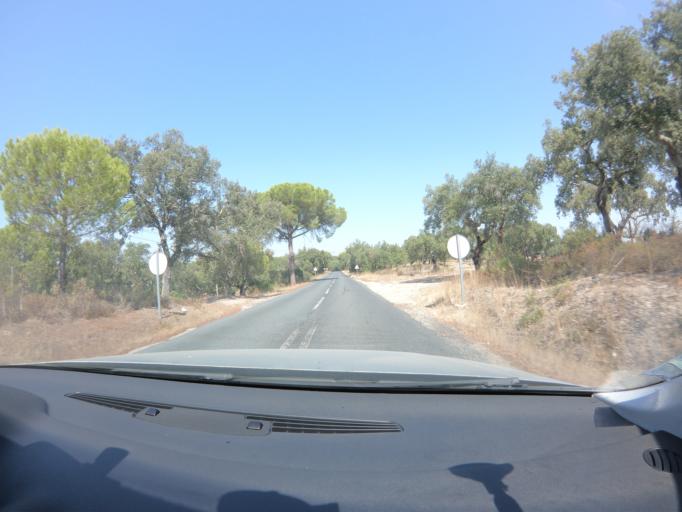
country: PT
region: Setubal
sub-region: Alcacer do Sal
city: Alcacer do Sal
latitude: 38.2982
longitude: -8.4043
